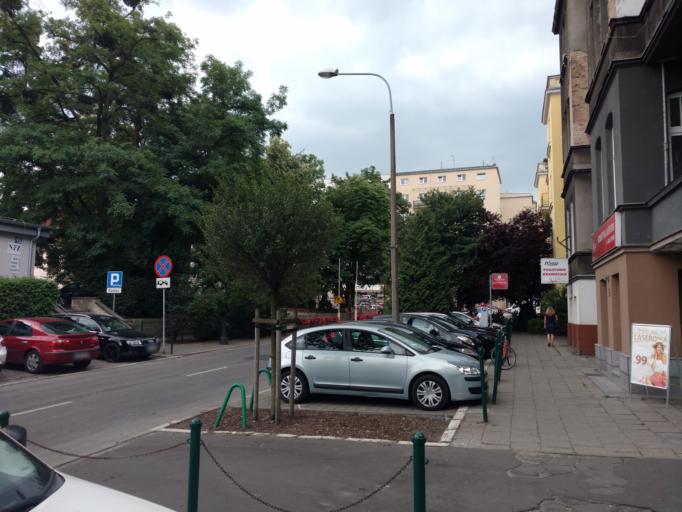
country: PL
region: Greater Poland Voivodeship
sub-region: Poznan
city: Poznan
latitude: 52.4121
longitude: 16.9100
